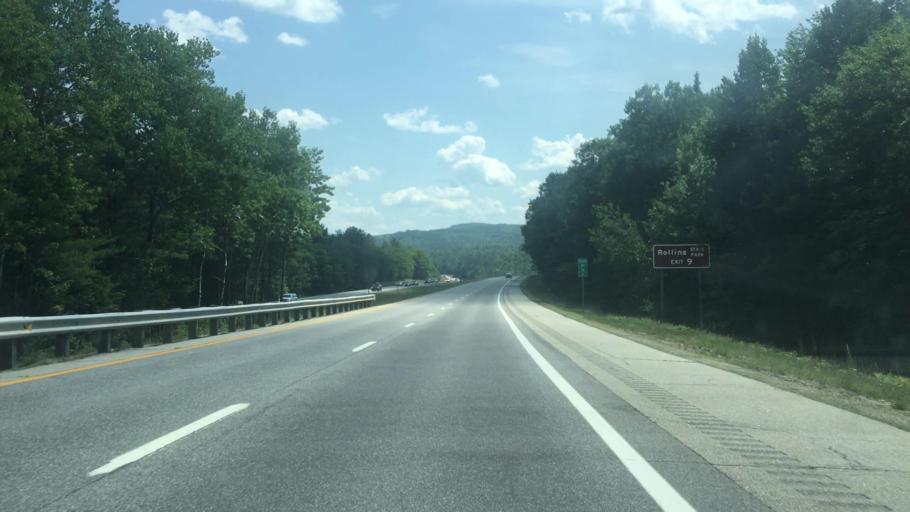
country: US
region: New Hampshire
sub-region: Merrimack County
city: Sutton
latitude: 43.2979
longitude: -71.8400
